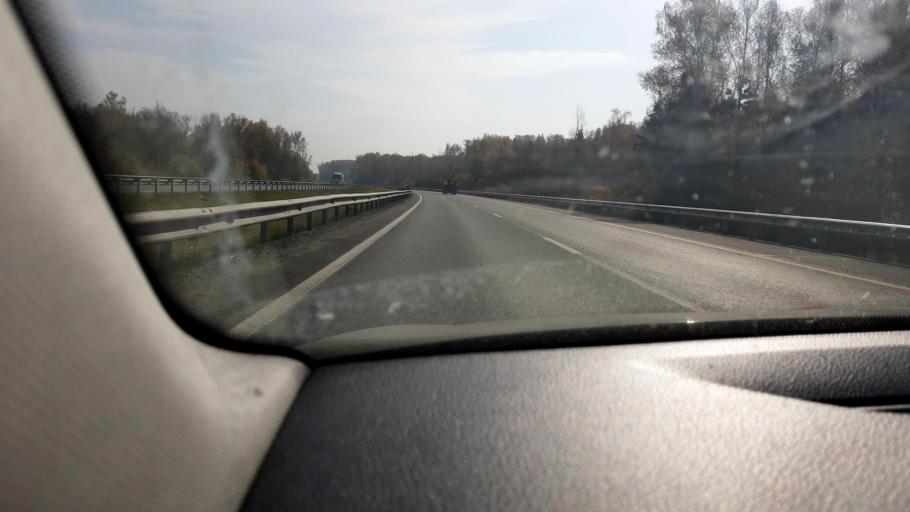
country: RU
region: Moskovskaya
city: Zhilevo
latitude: 55.0233
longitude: 37.9472
